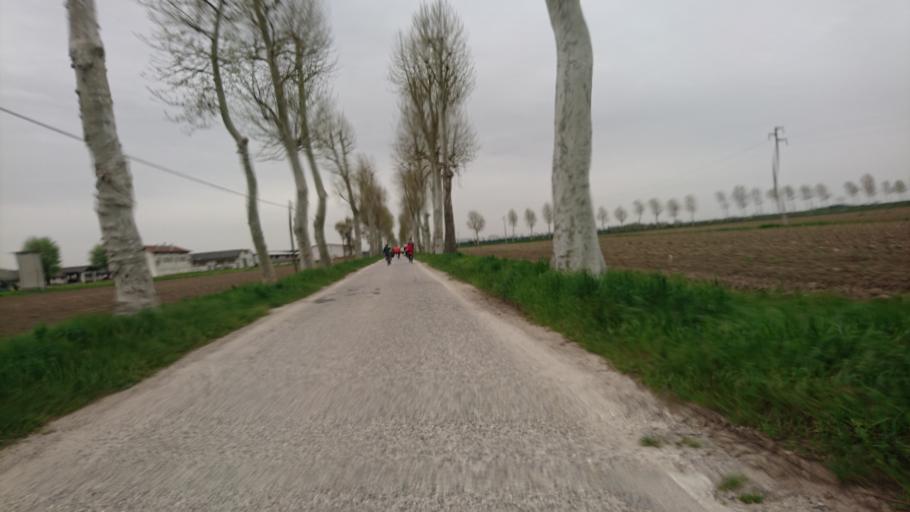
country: IT
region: Veneto
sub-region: Provincia di Venezia
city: Lugugnana
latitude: 45.6923
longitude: 12.9752
